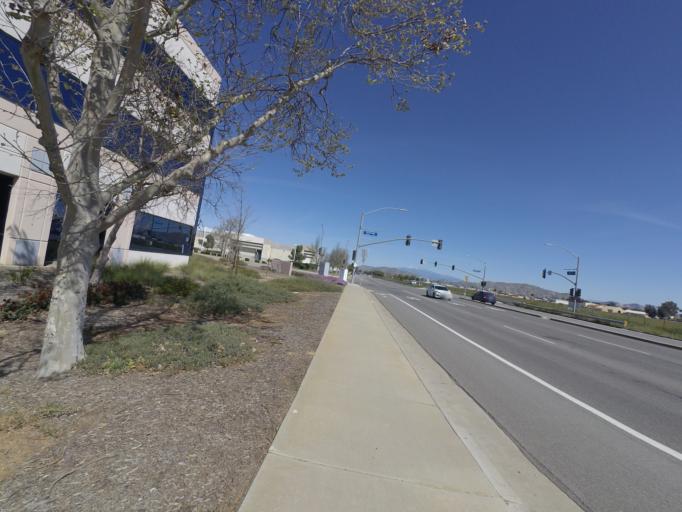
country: US
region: California
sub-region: Riverside County
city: March Air Force Base
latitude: 33.9102
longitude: -117.2674
